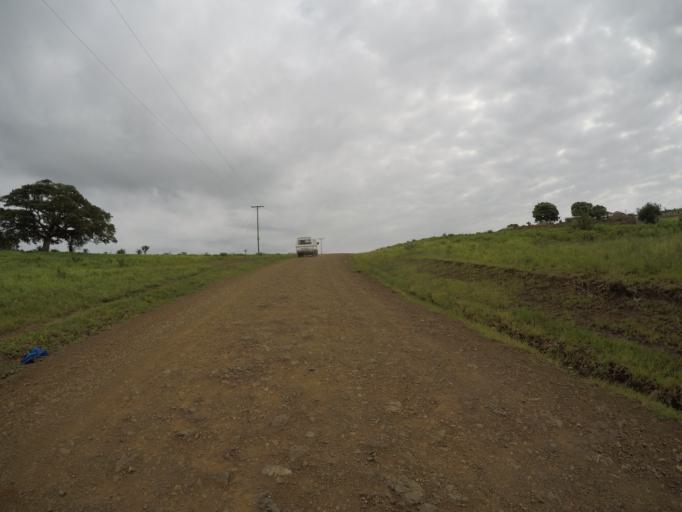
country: ZA
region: KwaZulu-Natal
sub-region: uThungulu District Municipality
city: Empangeni
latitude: -28.6374
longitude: 31.9046
